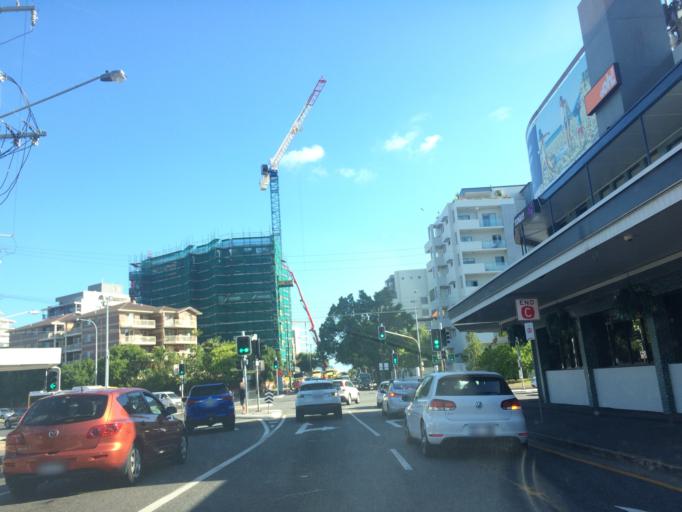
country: AU
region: Queensland
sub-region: Brisbane
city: Woolloongabba
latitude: -27.4794
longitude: 153.0414
